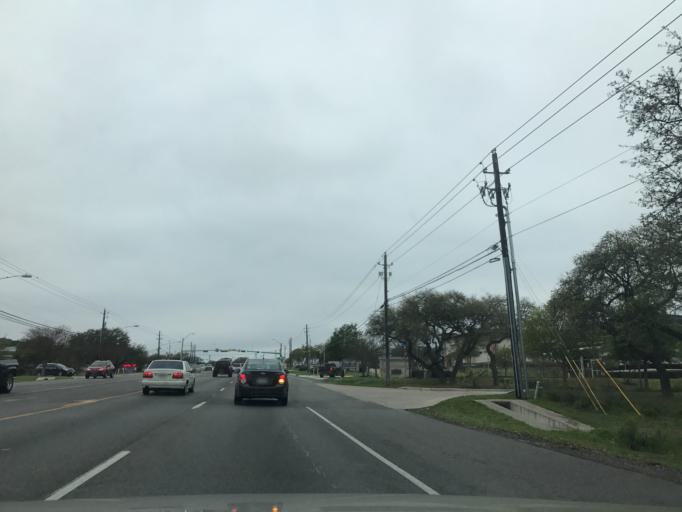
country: US
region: Texas
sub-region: Travis County
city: The Hills
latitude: 30.3424
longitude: -97.9676
